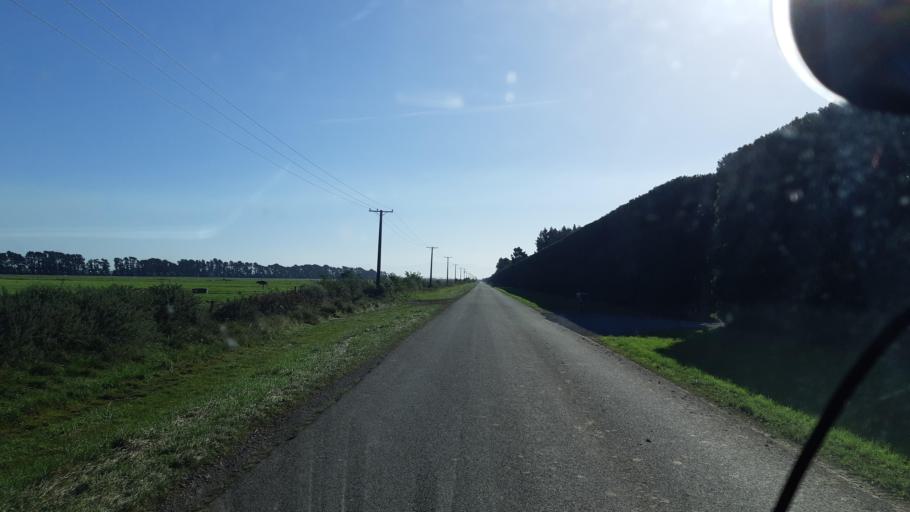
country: NZ
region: Canterbury
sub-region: Selwyn District
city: Burnham
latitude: -43.6388
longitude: 172.2398
